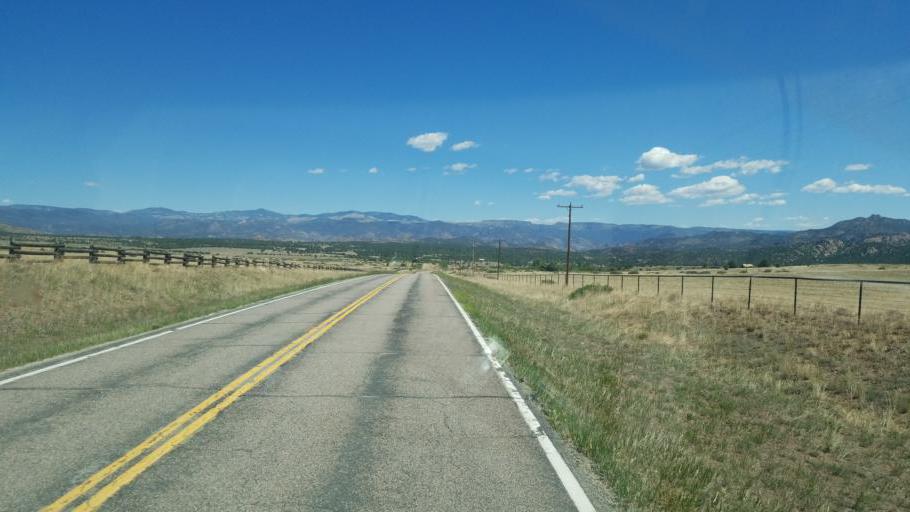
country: US
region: Colorado
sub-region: Custer County
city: Westcliffe
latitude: 38.2797
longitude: -105.6161
